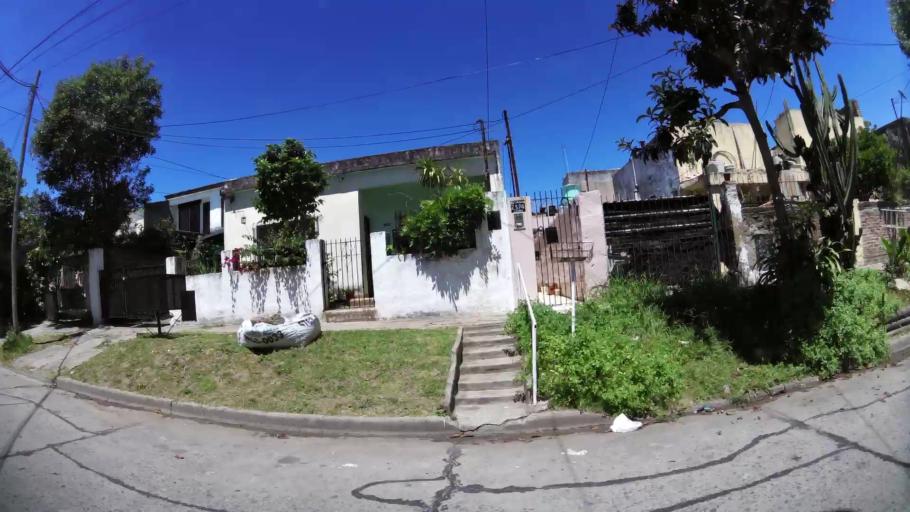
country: AR
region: Buenos Aires
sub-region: Partido de Tigre
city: Tigre
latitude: -34.4999
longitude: -58.5819
